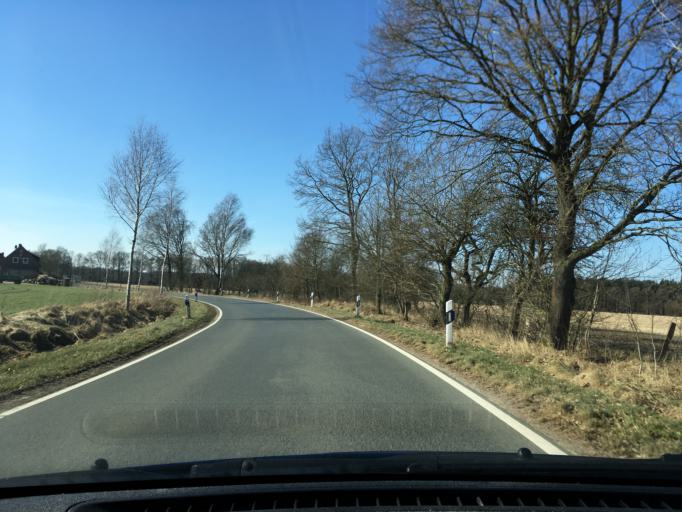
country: DE
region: Lower Saxony
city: Neuenkirchen
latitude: 53.0797
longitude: 9.7230
